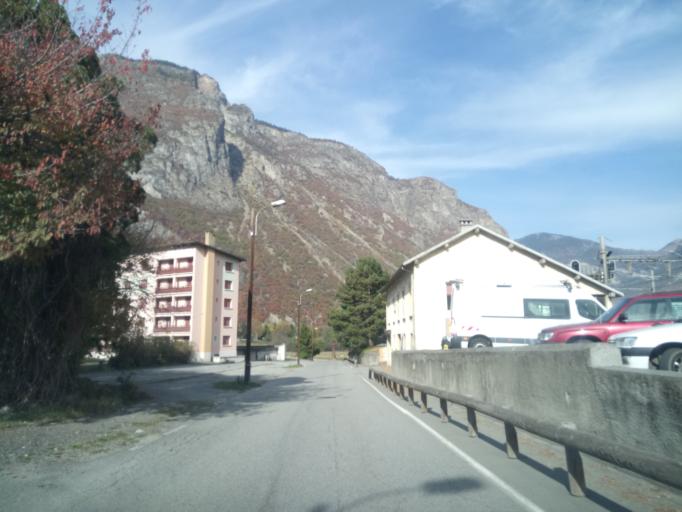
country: FR
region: Rhone-Alpes
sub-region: Departement de la Savoie
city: Saint-Jean-de-Maurienne
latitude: 45.2787
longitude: 6.3528
